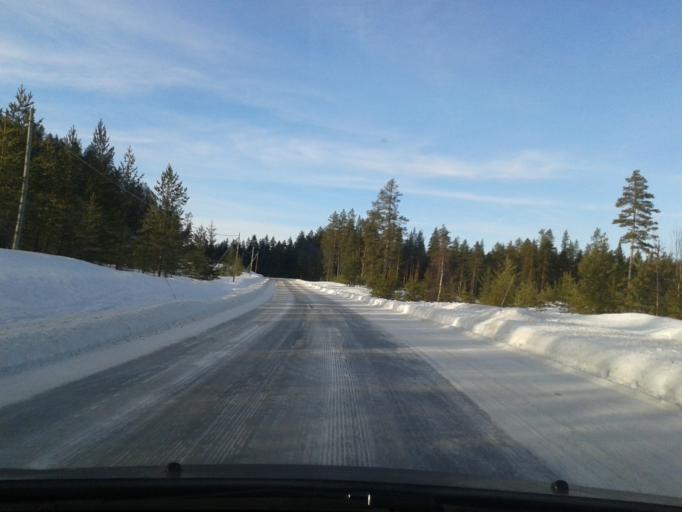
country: SE
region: Vaesternorrland
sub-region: OErnskoeldsviks Kommun
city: Bredbyn
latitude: 63.6718
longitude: 17.8232
